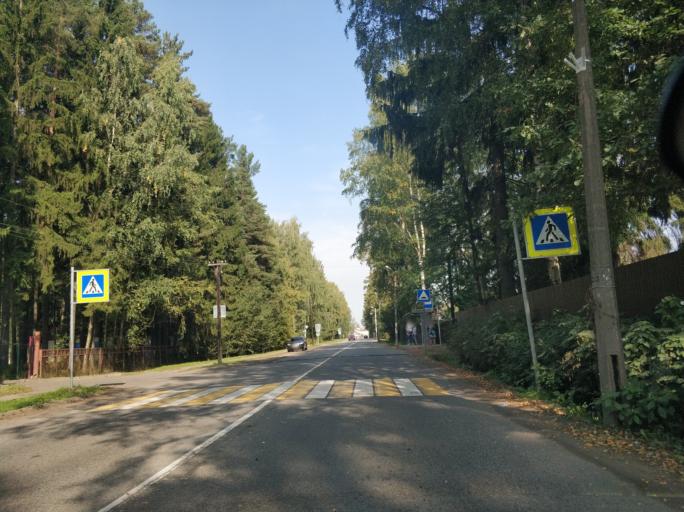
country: RU
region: Leningrad
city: Vsevolozhsk
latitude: 60.0123
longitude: 30.6208
